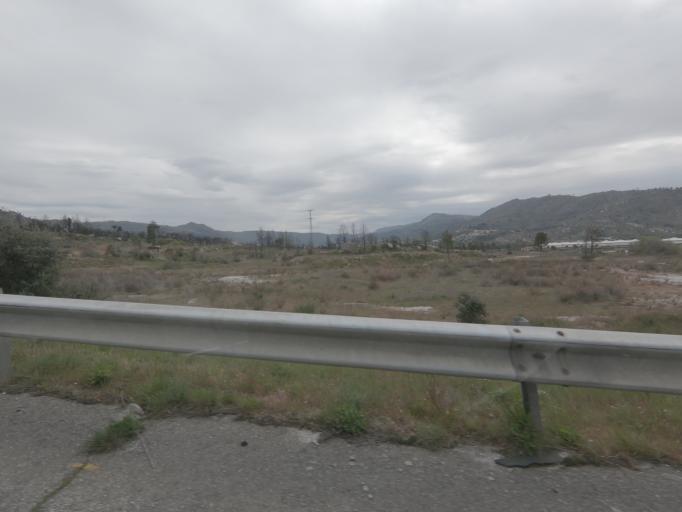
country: PT
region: Guarda
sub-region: Guarda
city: Guarda
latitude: 40.6211
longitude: -7.2907
